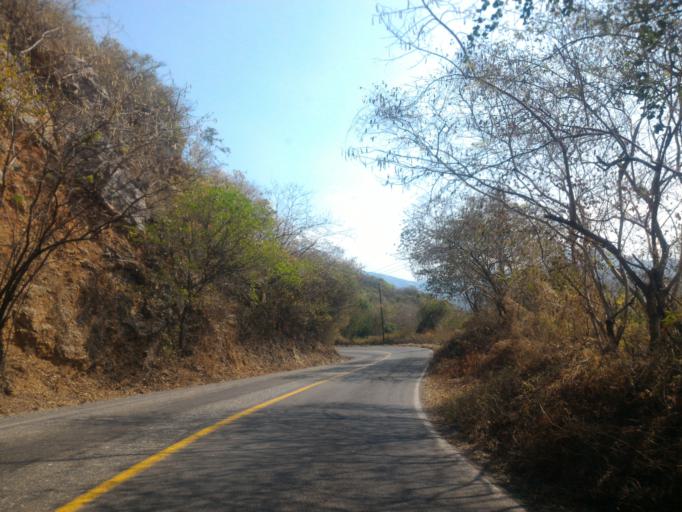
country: MX
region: Michoacan
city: Coahuayana Viejo
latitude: 18.5640
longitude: -103.6399
